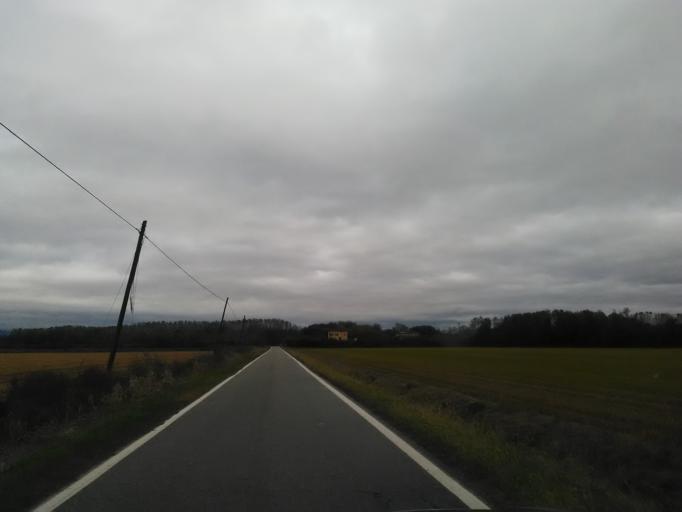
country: IT
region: Piedmont
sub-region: Provincia di Vercelli
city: Carisio
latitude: 45.3983
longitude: 8.2435
